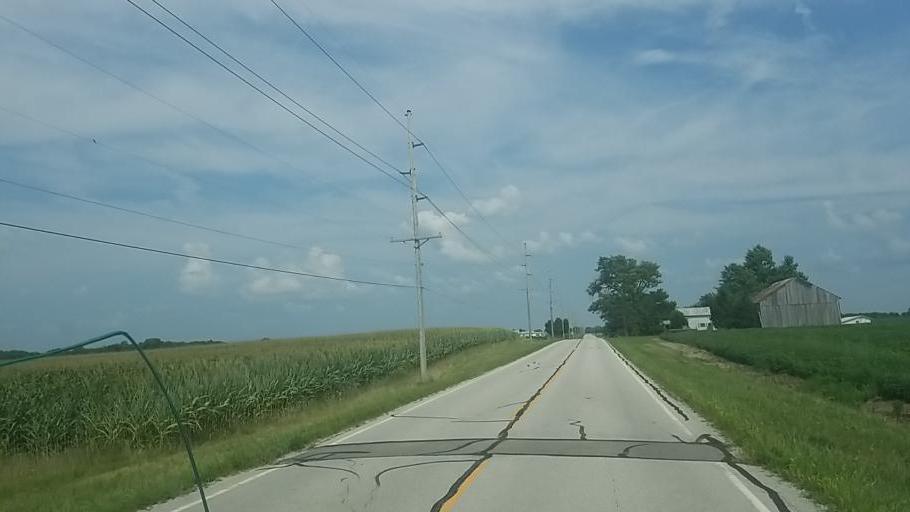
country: US
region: Ohio
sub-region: Hardin County
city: Forest
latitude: 40.7819
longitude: -83.5517
